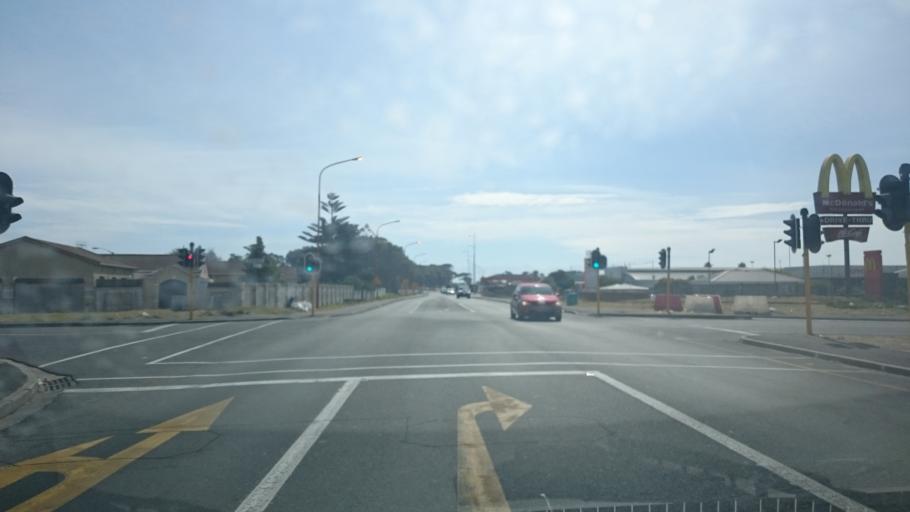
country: ZA
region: Western Cape
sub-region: City of Cape Town
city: Lansdowne
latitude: -34.0175
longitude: 18.5154
